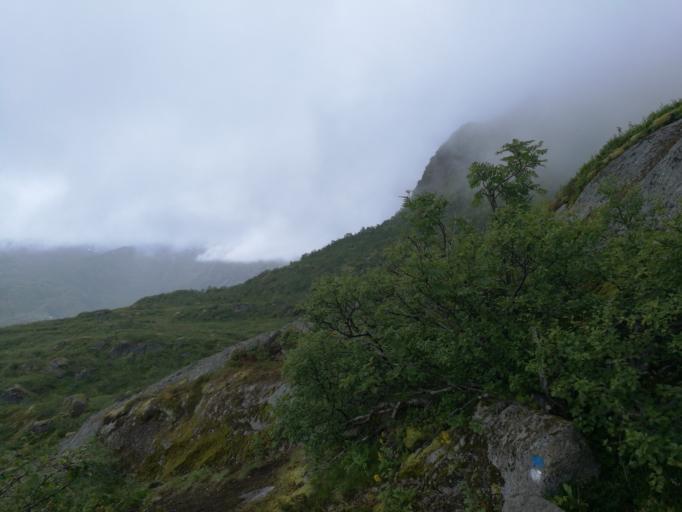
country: NO
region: Nordland
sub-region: Vagan
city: Svolvaer
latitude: 68.2488
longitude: 14.5846
